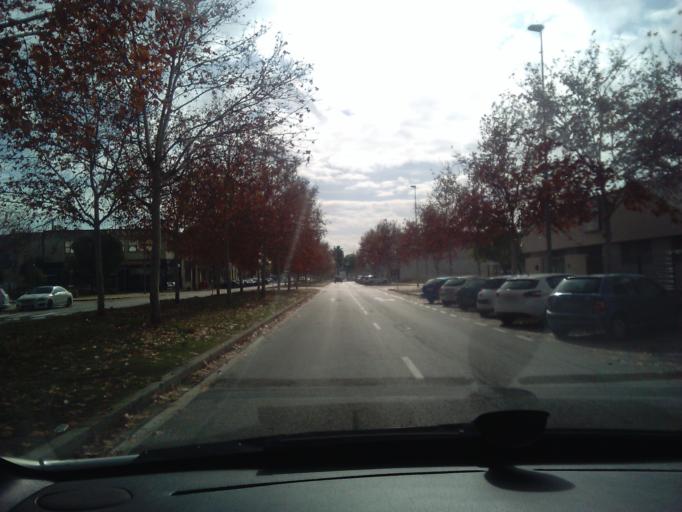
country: ES
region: Andalusia
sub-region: Provincia de Sevilla
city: Sevilla
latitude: 37.3781
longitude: -5.9193
